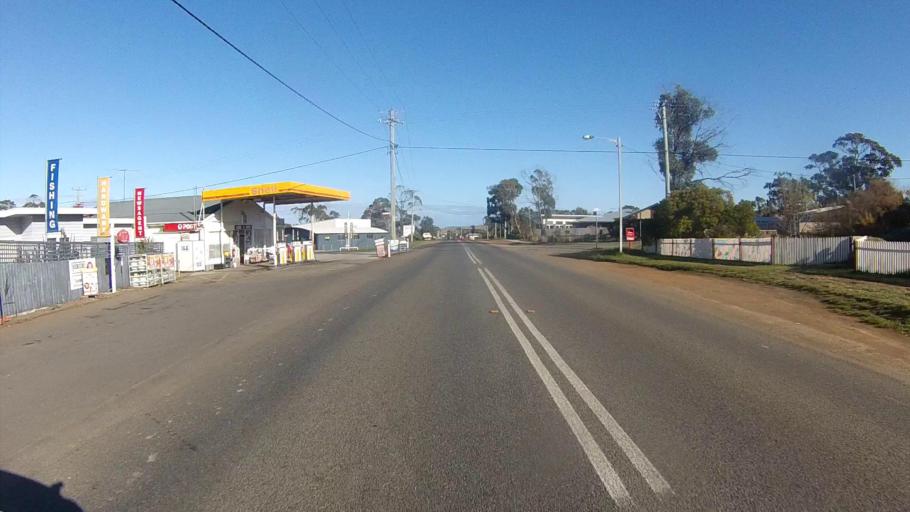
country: AU
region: Tasmania
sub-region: Sorell
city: Sorell
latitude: -42.8849
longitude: 147.8138
